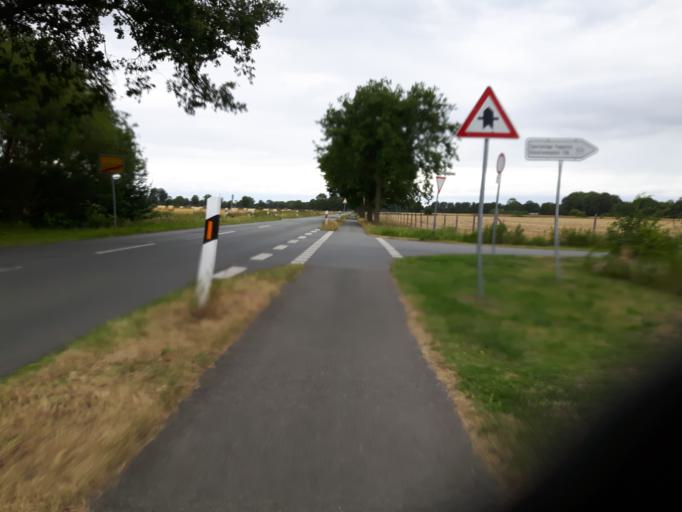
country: DE
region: Lower Saxony
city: Stuhr
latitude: 53.0057
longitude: 8.7732
